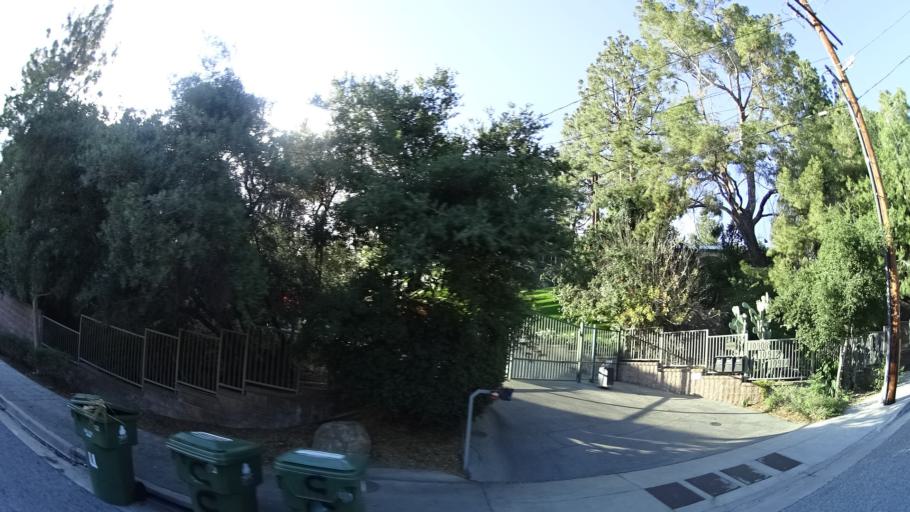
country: US
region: California
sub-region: Los Angeles County
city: La Crescenta-Montrose
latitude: 34.2676
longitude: -118.2949
